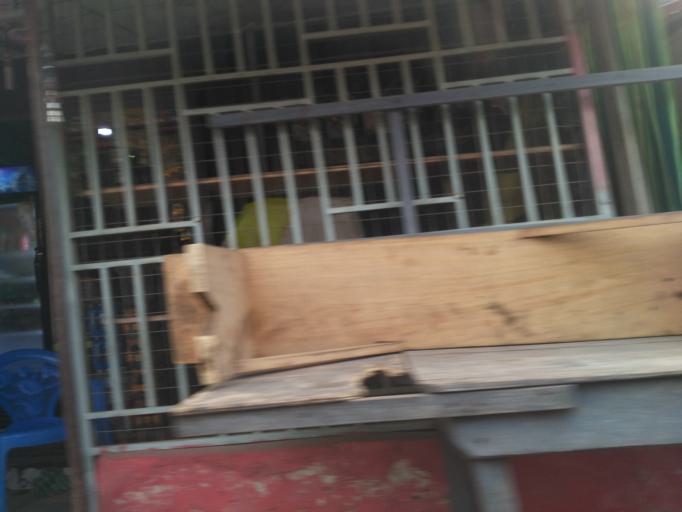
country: GH
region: Ashanti
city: Kumasi
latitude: 6.6744
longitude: -1.5922
